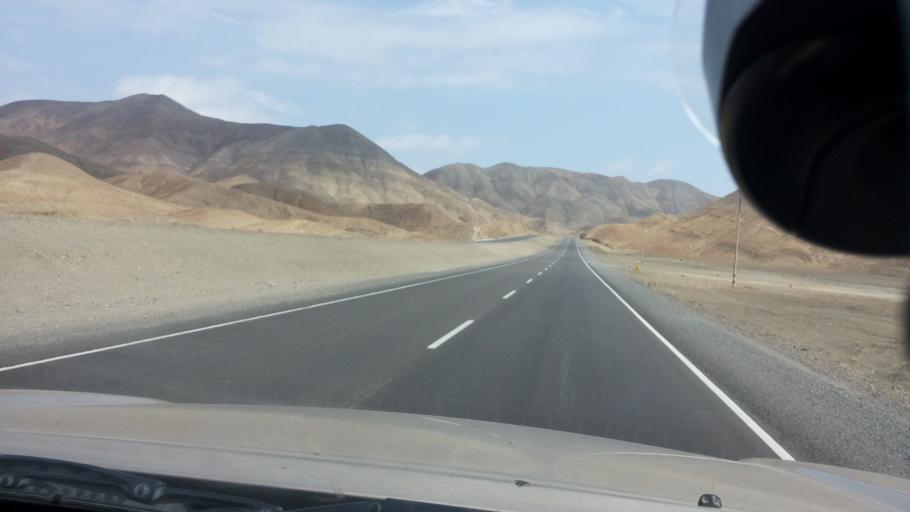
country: PE
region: Ancash
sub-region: Provincia de Huarmey
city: La Caleta Culebras
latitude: -9.8894
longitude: -78.2101
